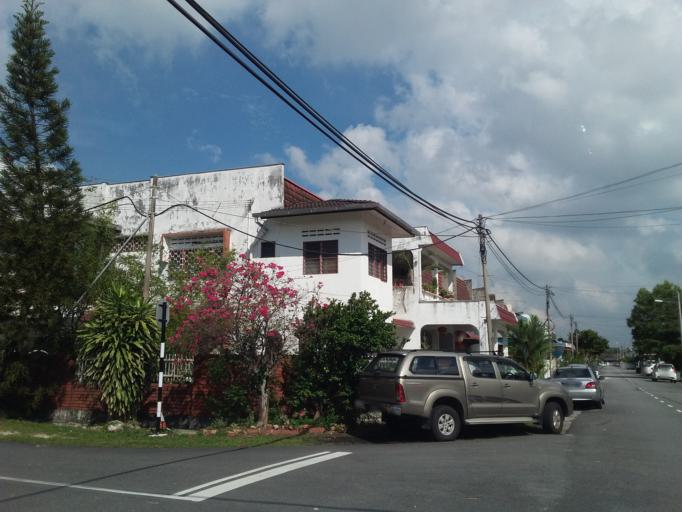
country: MY
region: Johor
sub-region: Daerah Batu Pahat
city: Batu Pahat
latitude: 1.8409
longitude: 102.9293
